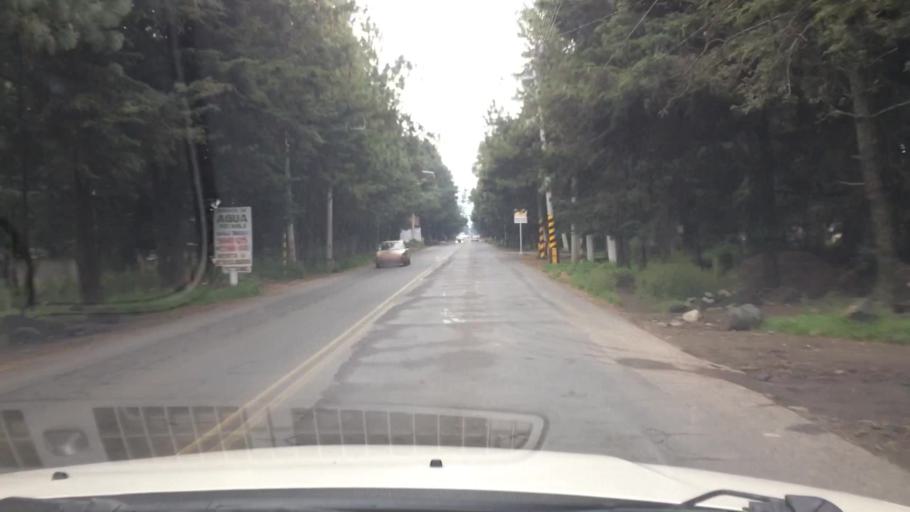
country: MX
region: Mexico City
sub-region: Tlalpan
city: Lomas de Tepemecatl
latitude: 19.2417
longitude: -99.2390
